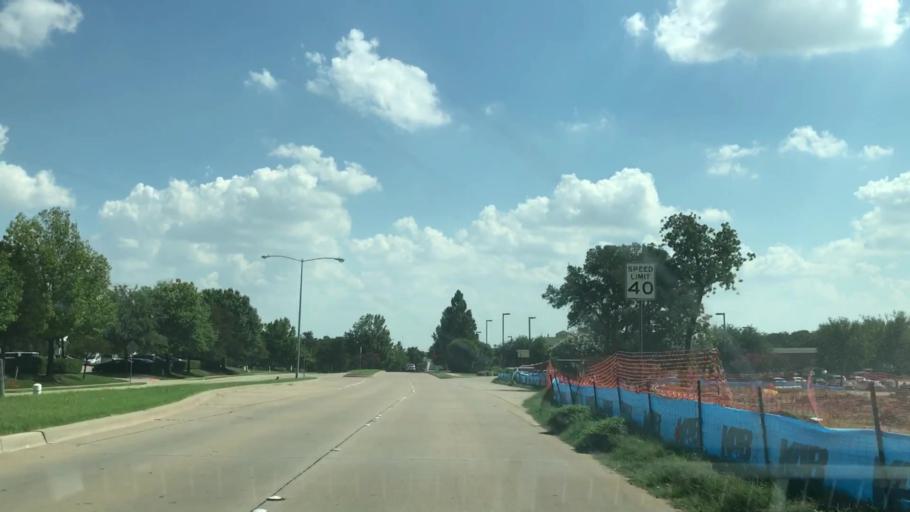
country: US
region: Texas
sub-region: Denton County
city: Lewisville
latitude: 33.0189
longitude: -96.9797
